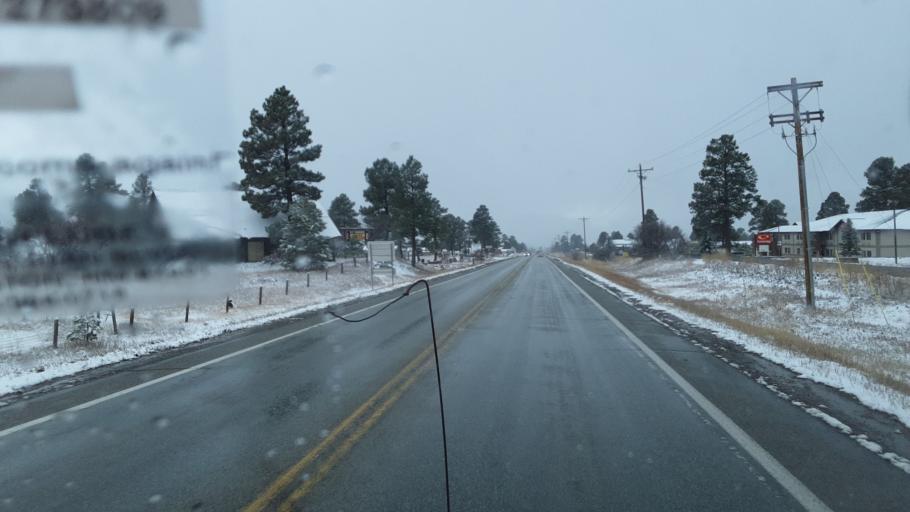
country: US
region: Colorado
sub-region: Archuleta County
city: Pagosa Springs
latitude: 37.2524
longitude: -107.0811
